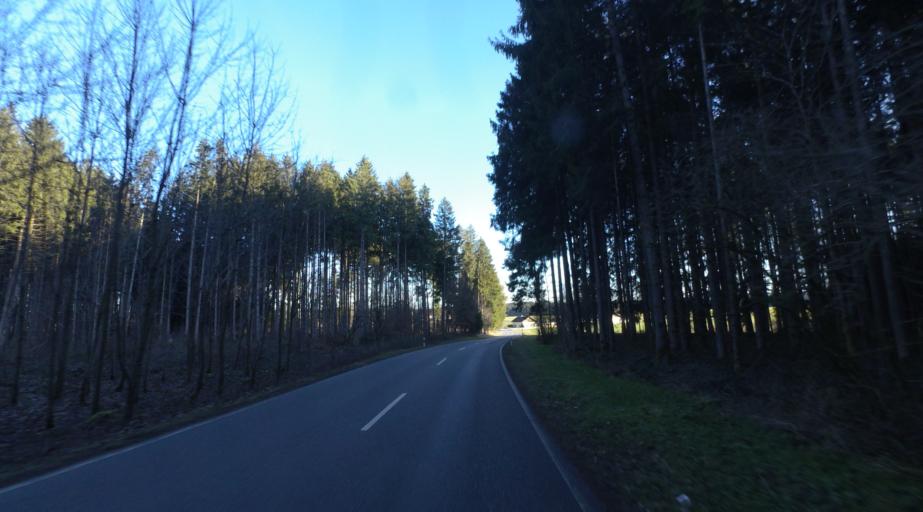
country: DE
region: Bavaria
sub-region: Upper Bavaria
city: Trostberg an der Alz
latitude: 48.0216
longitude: 12.5813
